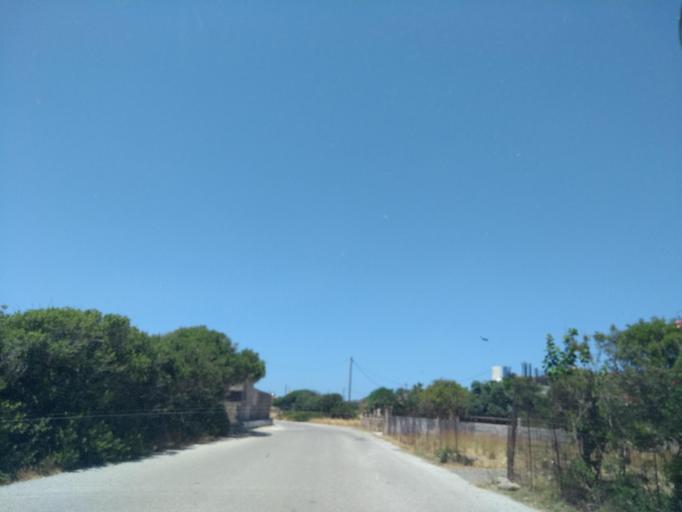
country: GR
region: Crete
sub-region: Nomos Chanias
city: Vryses
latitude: 35.3582
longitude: 23.5322
